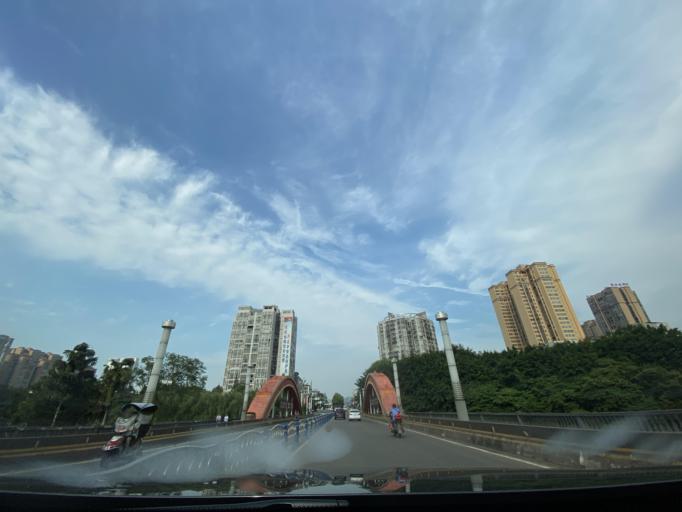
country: CN
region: Sichuan
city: Fuji
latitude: 29.1536
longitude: 105.3622
